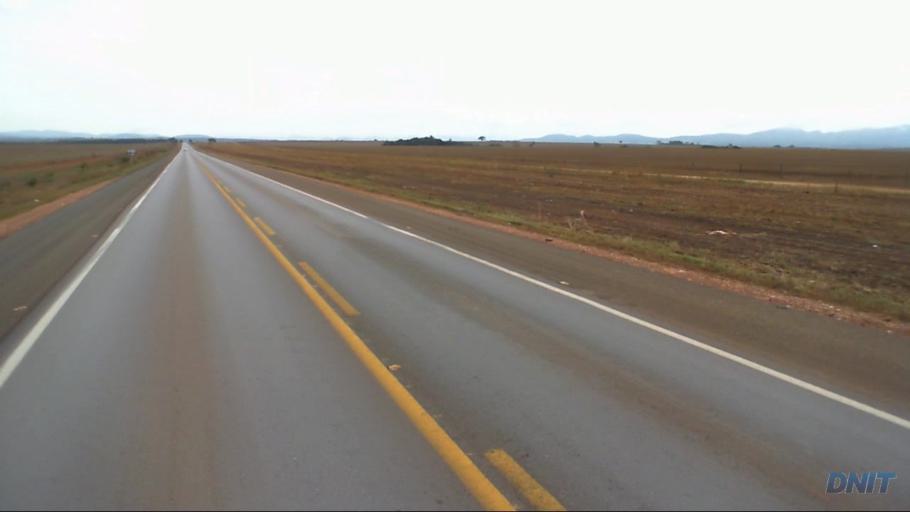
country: BR
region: Goias
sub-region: Uruacu
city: Uruacu
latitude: -14.6513
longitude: -49.1626
